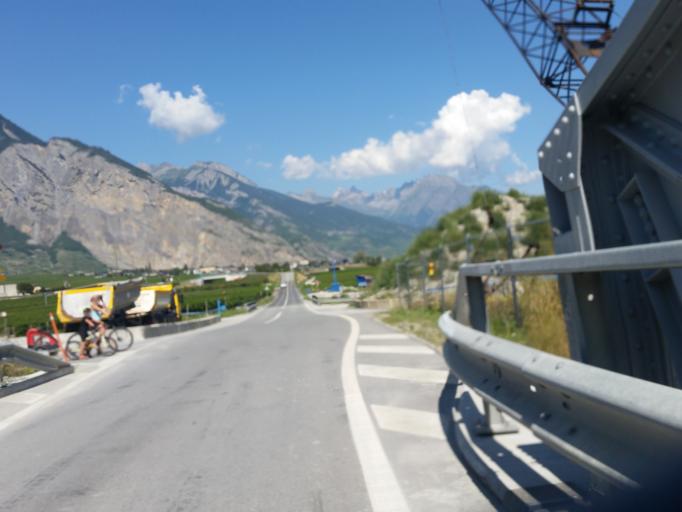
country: CH
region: Valais
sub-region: Martigny District
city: Riddes
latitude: 46.1775
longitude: 7.2281
